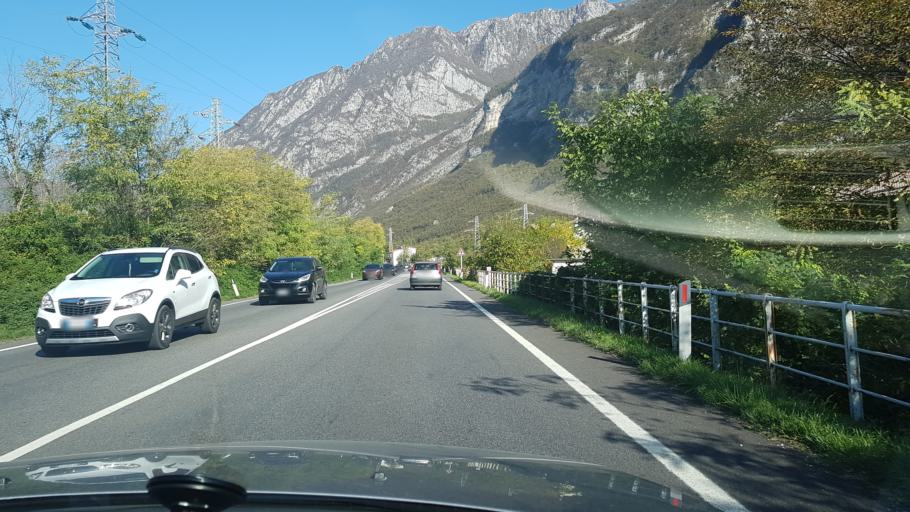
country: IT
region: Friuli Venezia Giulia
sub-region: Provincia di Udine
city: Venzone
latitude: 46.3365
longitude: 13.1387
